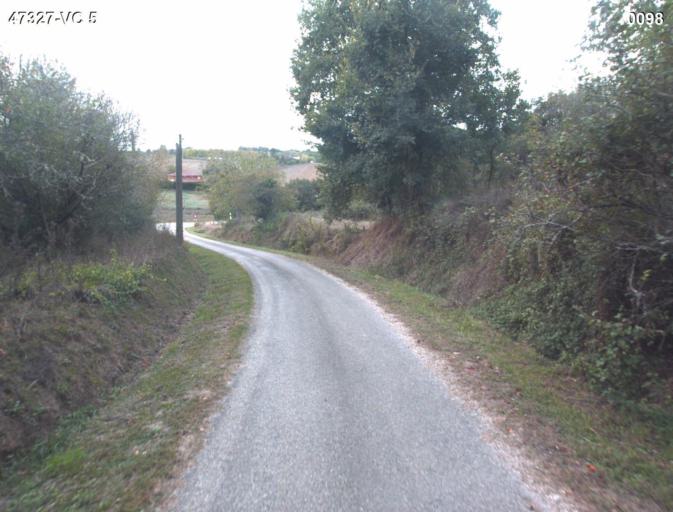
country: FR
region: Aquitaine
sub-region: Departement du Lot-et-Garonne
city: Buzet-sur-Baise
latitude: 44.2195
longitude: 0.2710
